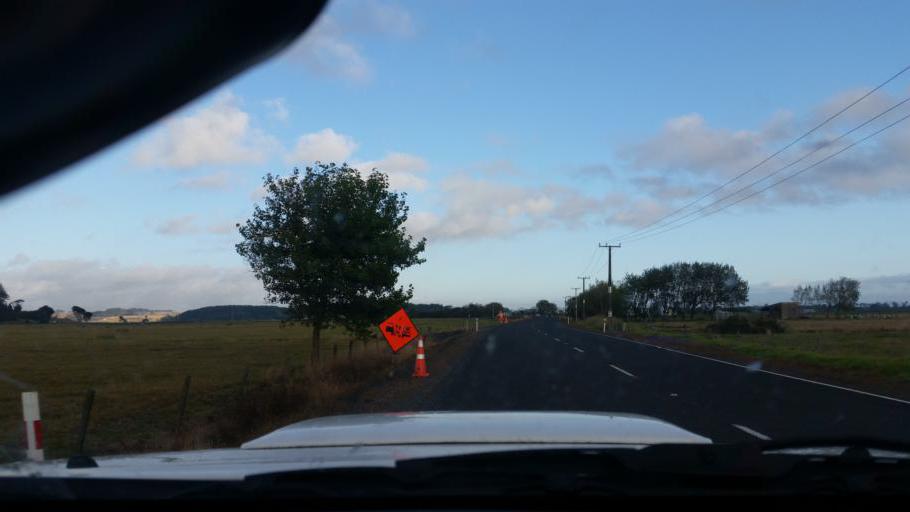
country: NZ
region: Northland
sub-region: Kaipara District
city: Dargaville
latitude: -36.0080
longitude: 173.8961
